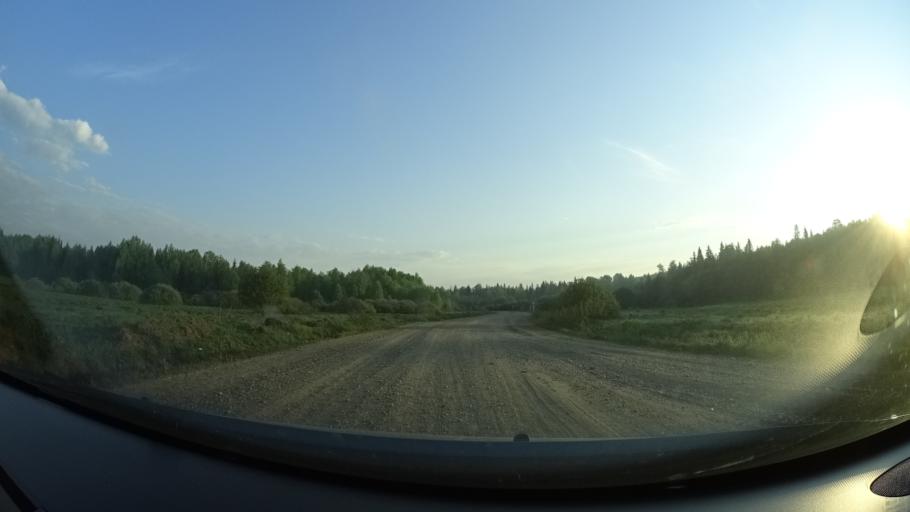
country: RU
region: Perm
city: Kuyeda
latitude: 56.6194
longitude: 55.7104
